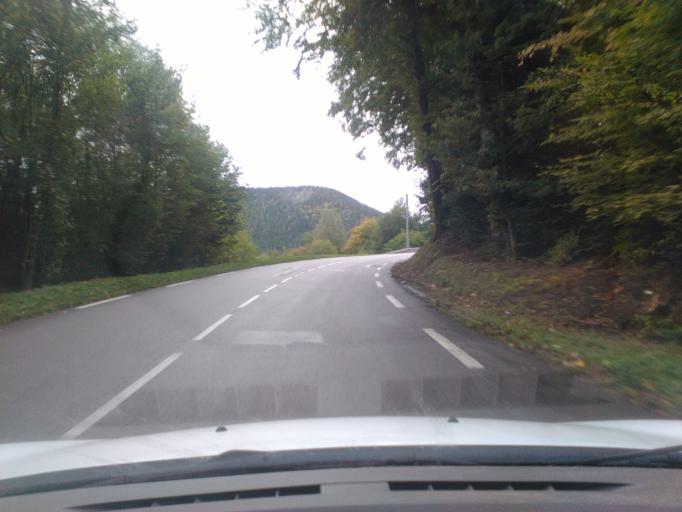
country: FR
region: Lorraine
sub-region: Departement des Vosges
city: Taintrux
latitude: 48.2761
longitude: 6.8908
